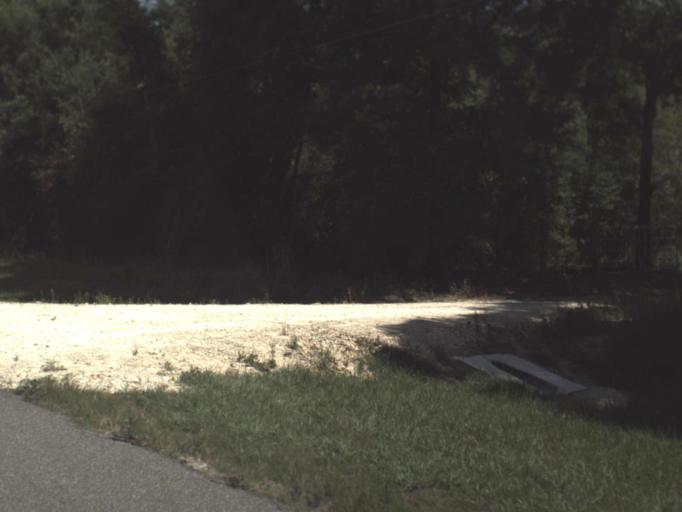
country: US
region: Florida
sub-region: Lafayette County
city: Mayo
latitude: 30.0112
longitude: -83.0345
